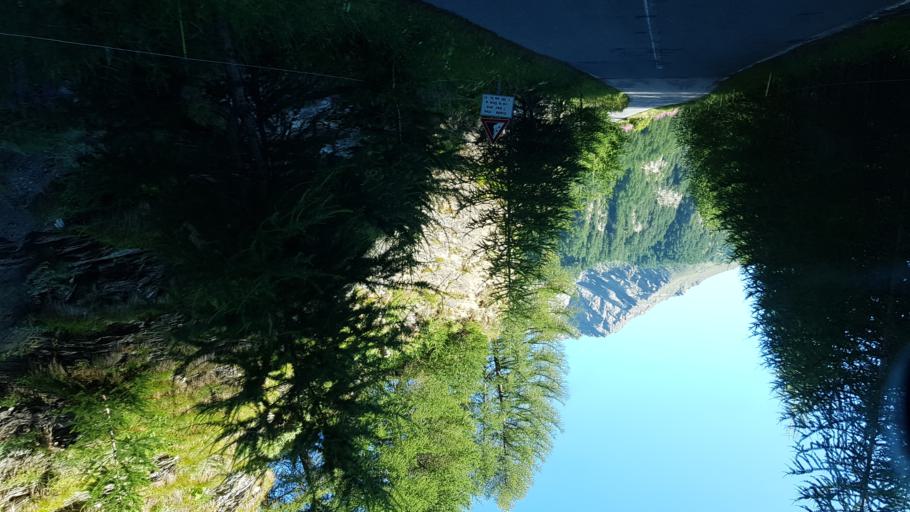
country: IT
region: Piedmont
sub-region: Provincia di Cuneo
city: Pontechianale
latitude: 44.6550
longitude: 6.9904
